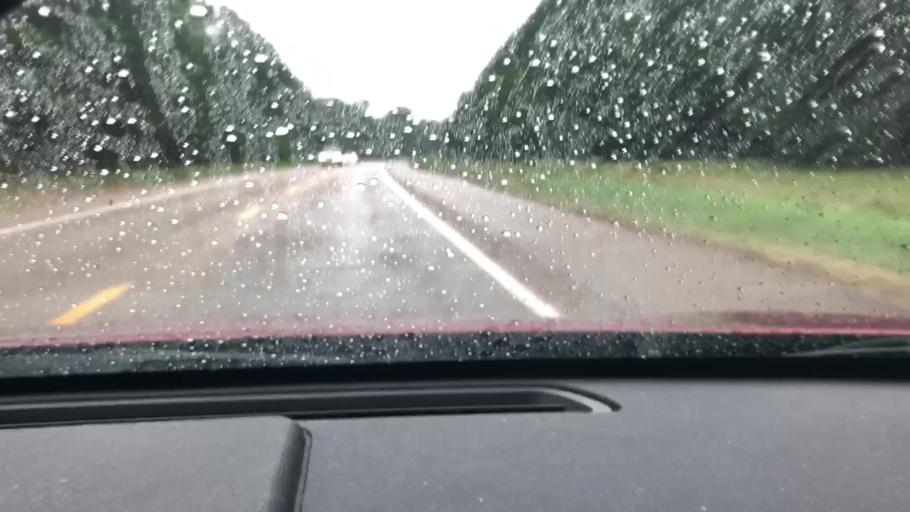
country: US
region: Arkansas
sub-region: Columbia County
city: Magnolia
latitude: 33.2973
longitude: -93.2601
